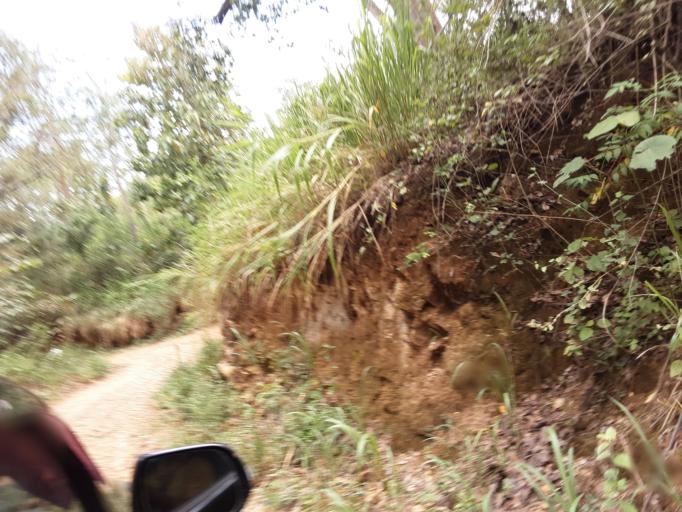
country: LK
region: Uva
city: Haputale
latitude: 6.8178
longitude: 81.1093
